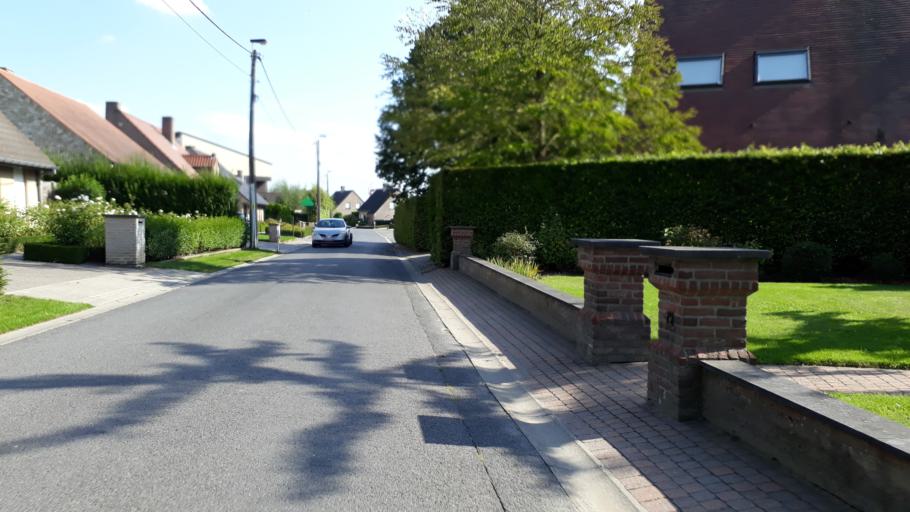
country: BE
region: Flanders
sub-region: Provincie West-Vlaanderen
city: Torhout
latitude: 51.0737
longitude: 3.0824
